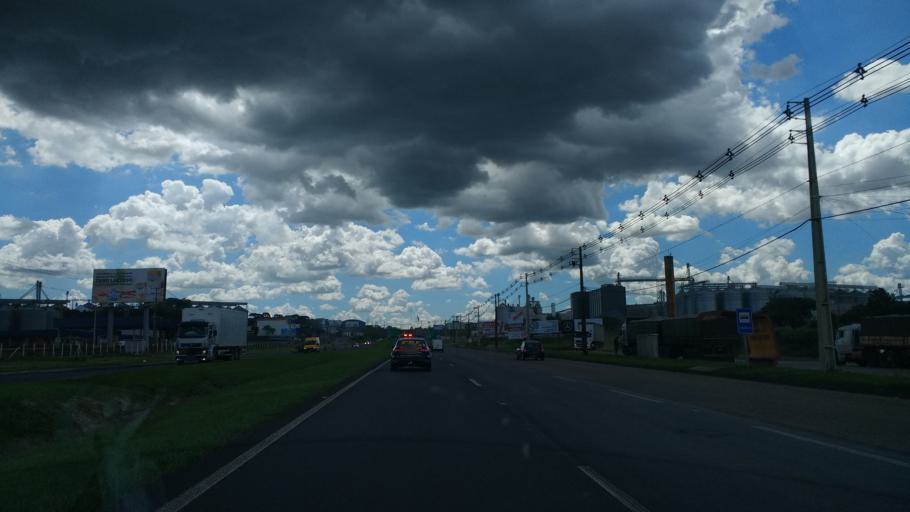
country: BR
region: Parana
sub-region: Ponta Grossa
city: Ponta Grossa
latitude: -25.1555
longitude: -50.1329
